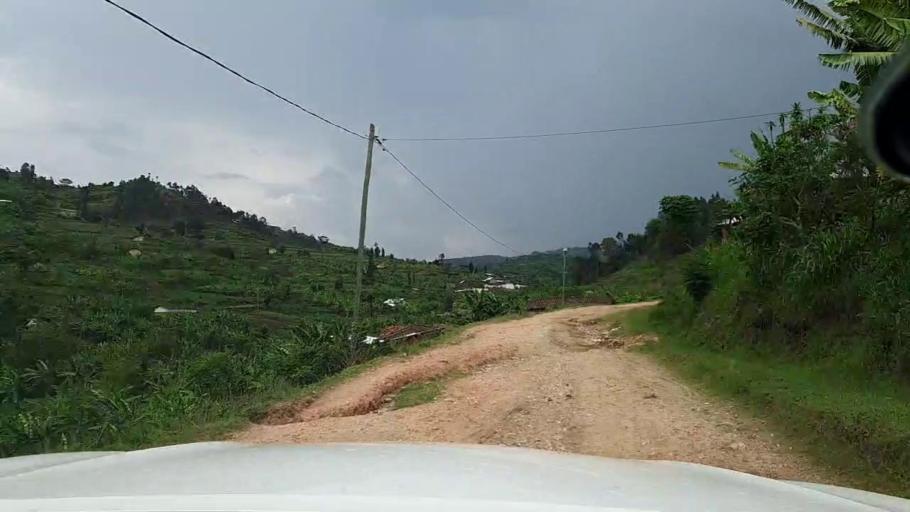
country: RW
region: Western Province
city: Kibuye
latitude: -2.0747
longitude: 29.4382
